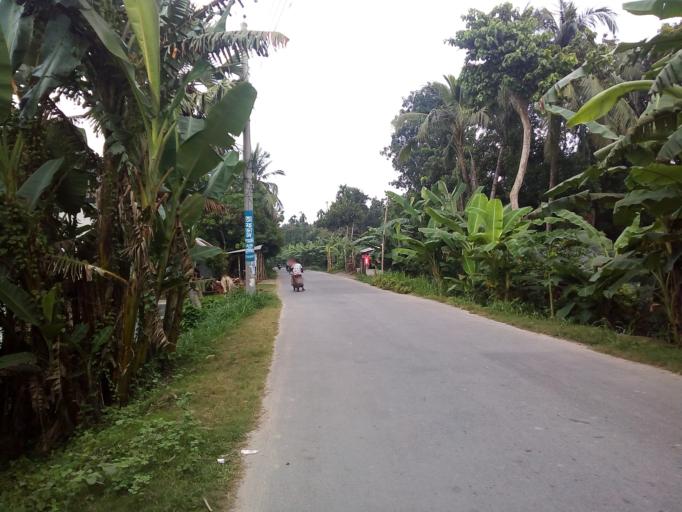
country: BD
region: Dhaka
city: Faridpur
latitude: 23.5534
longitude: 89.6311
